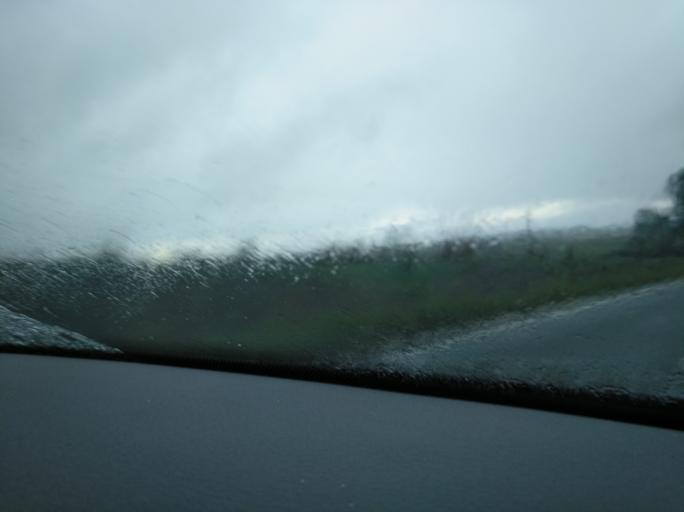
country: PT
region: Beja
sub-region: Castro Verde
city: Castro Verde
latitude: 37.7019
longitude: -7.9475
